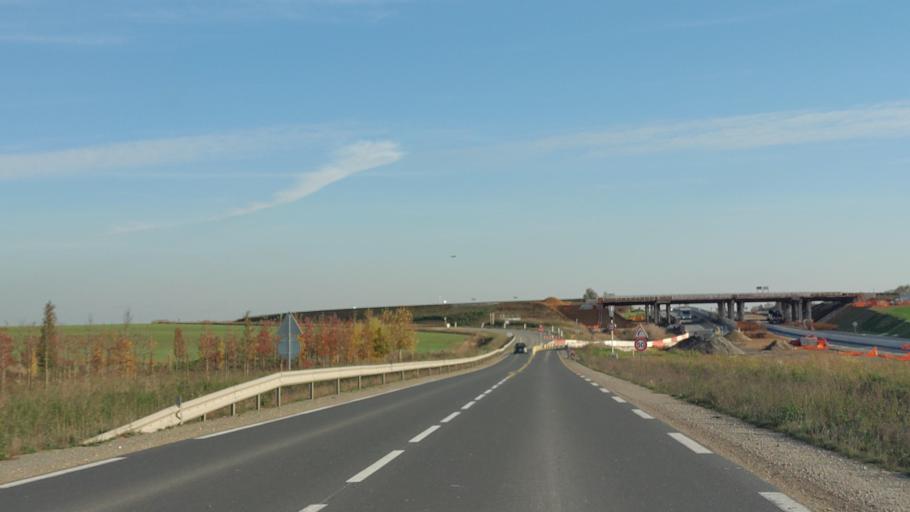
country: FR
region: Ile-de-France
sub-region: Departement de Seine-et-Marne
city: Mitry-Mory
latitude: 49.0122
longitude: 2.6076
